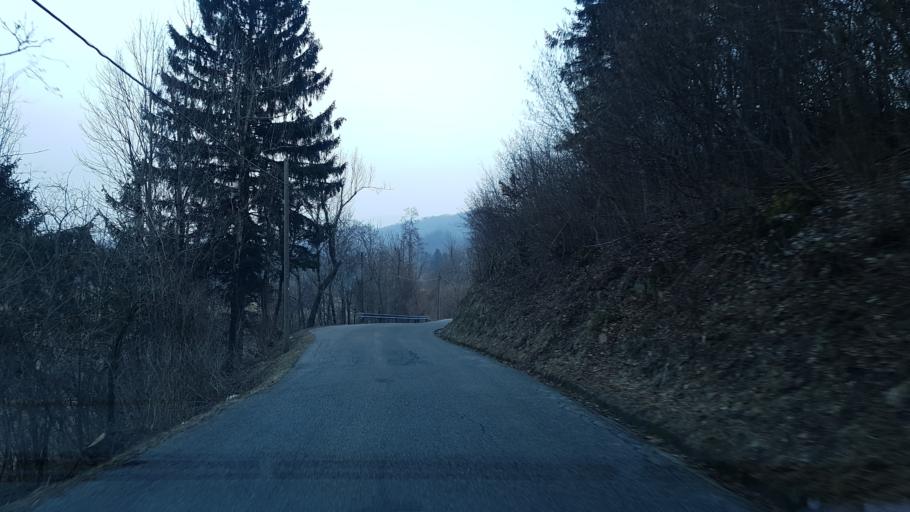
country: IT
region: Friuli Venezia Giulia
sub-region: Provincia di Udine
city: Taipana
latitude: 46.2566
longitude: 13.3612
